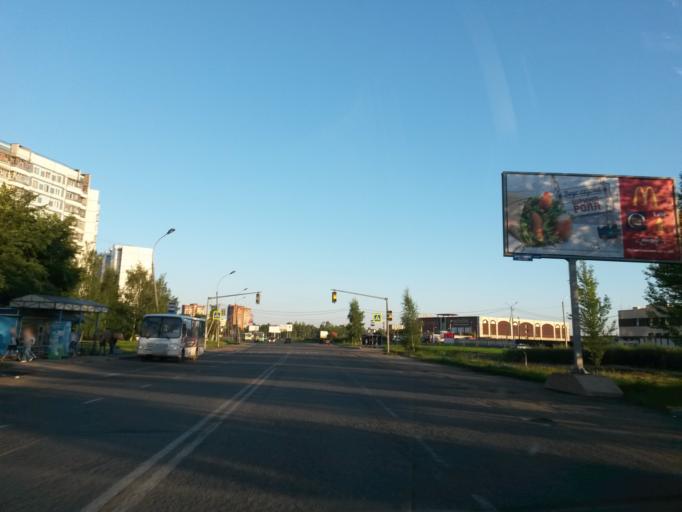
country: RU
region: Jaroslavl
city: Yaroslavl
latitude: 57.7021
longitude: 39.7596
